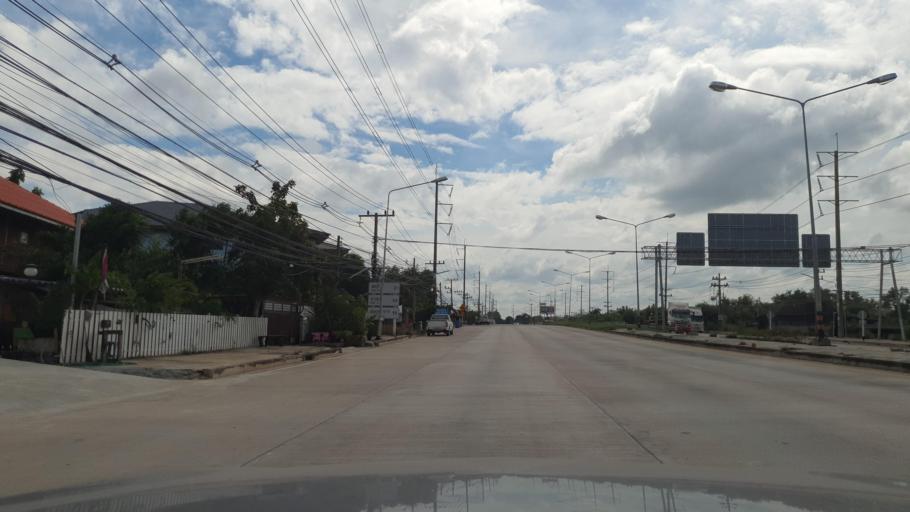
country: TH
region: Chachoengsao
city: Bang Pakong
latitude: 13.5445
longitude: 100.9897
